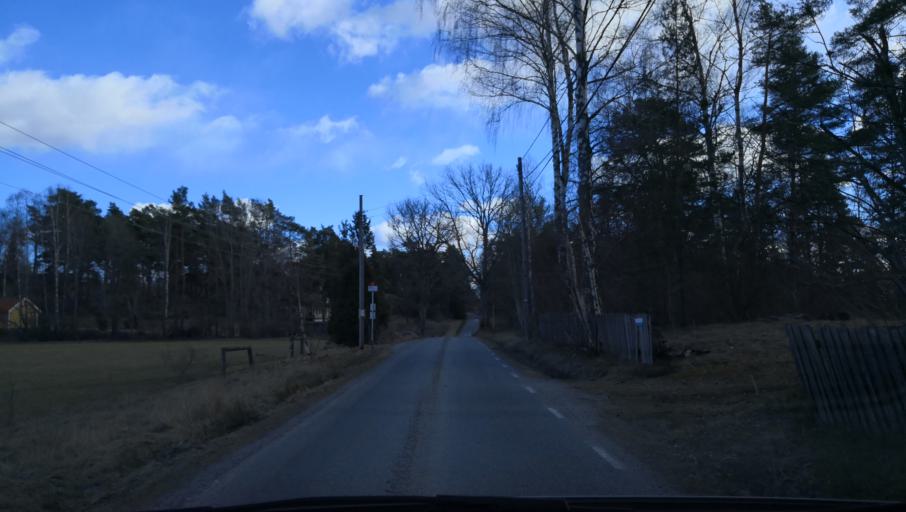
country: SE
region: Stockholm
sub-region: Varmdo Kommun
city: Mortnas
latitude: 59.3829
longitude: 18.4555
